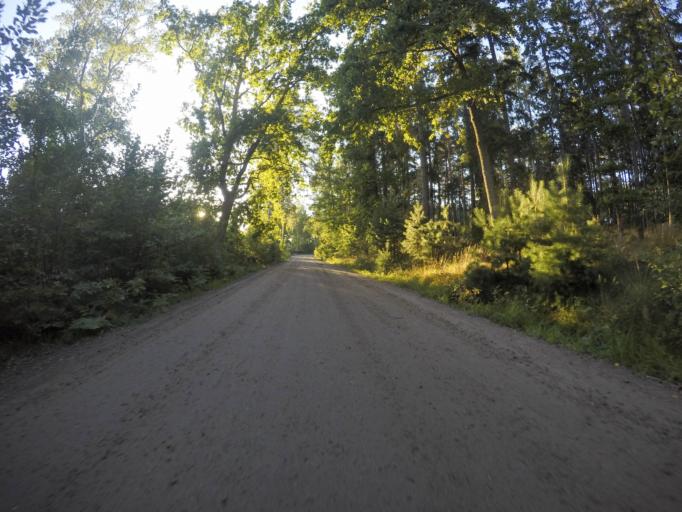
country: SE
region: Vaestmanland
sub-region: Vasteras
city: Vasteras
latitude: 59.5530
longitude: 16.6706
